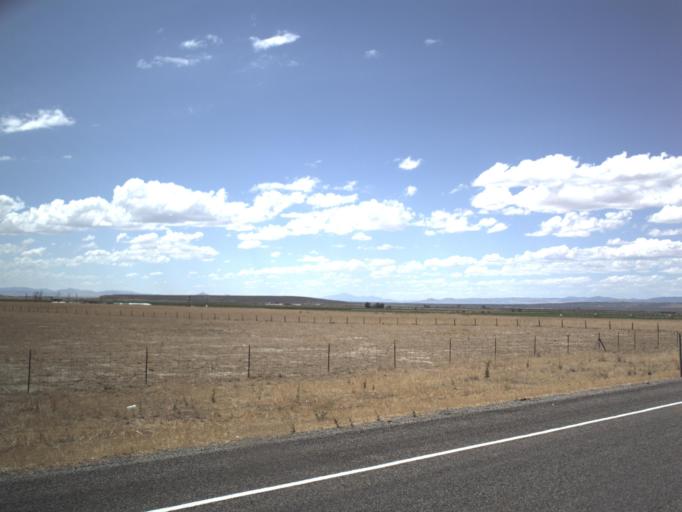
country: US
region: Utah
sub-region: Millard County
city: Fillmore
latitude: 39.1181
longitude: -112.3216
